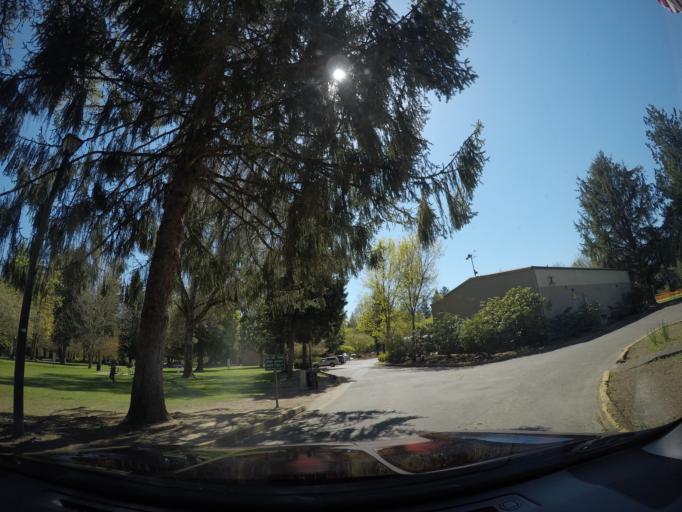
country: US
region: Oregon
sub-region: Washington County
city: Tualatin
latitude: 45.3967
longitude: -122.7723
